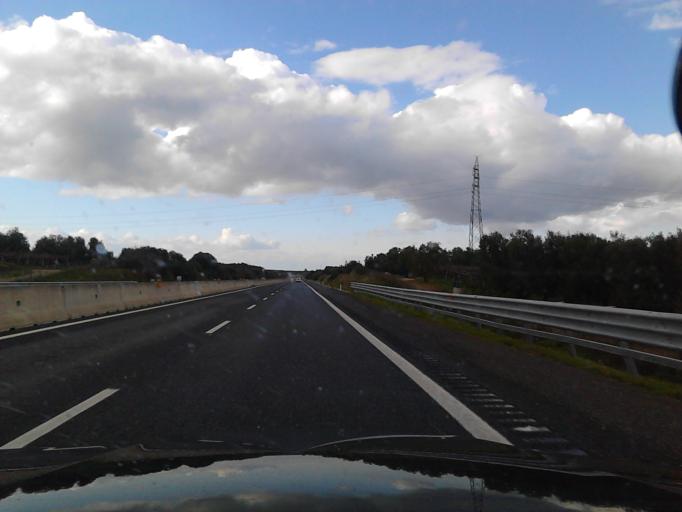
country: IT
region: Apulia
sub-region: Provincia di Barletta - Andria - Trani
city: Andria
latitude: 41.2587
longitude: 16.2711
